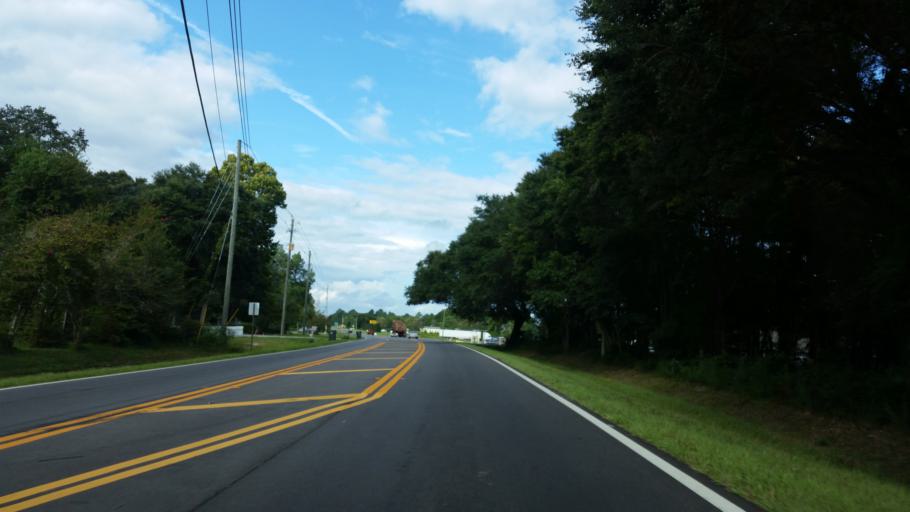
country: US
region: Florida
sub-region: Santa Rosa County
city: Wallace
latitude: 30.6474
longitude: -87.1634
